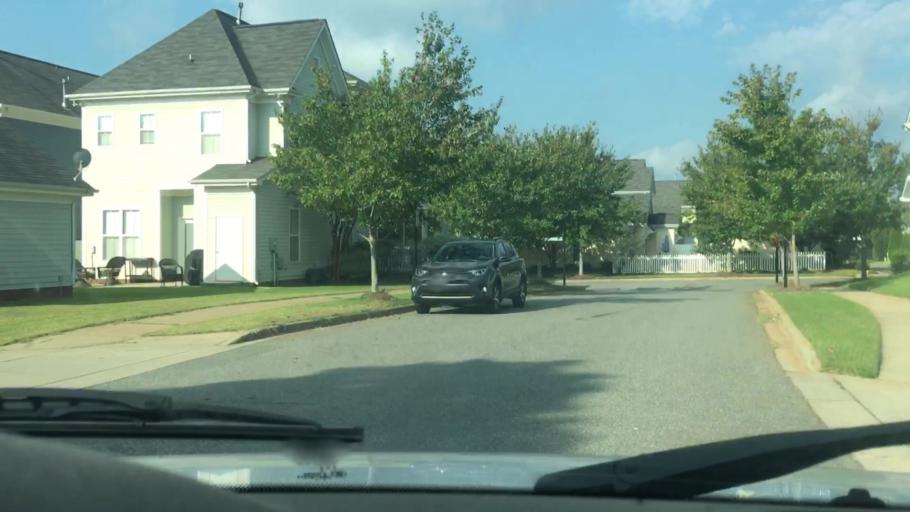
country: US
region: North Carolina
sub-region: Mecklenburg County
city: Huntersville
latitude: 35.4284
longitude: -80.8490
